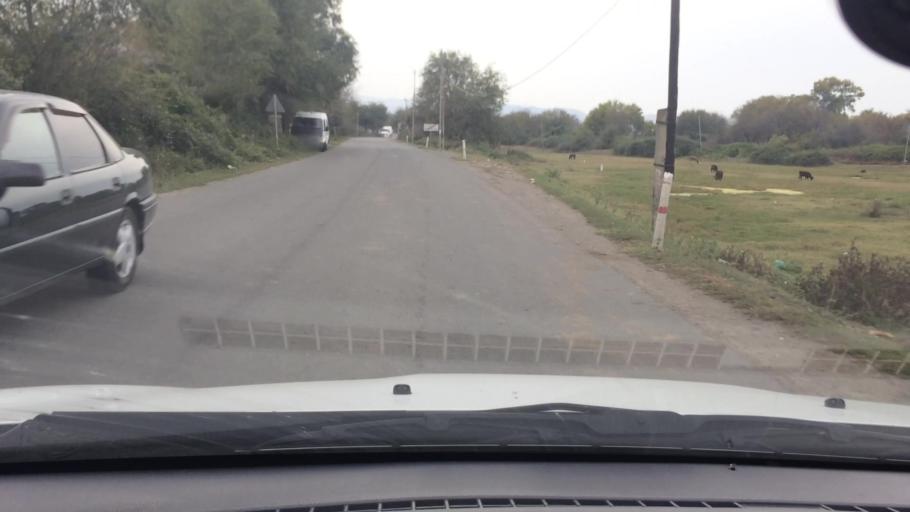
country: AM
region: Tavush
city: Bagratashen
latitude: 41.3406
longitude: 44.8886
